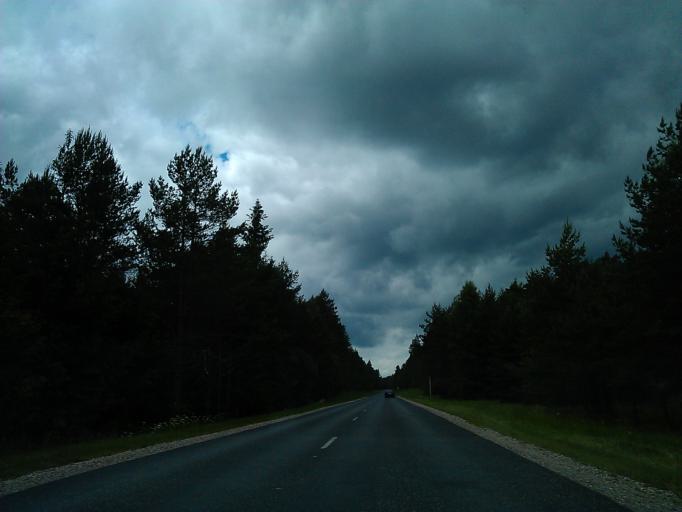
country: LV
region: Talsu Rajons
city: Stende
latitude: 57.0886
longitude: 22.4052
